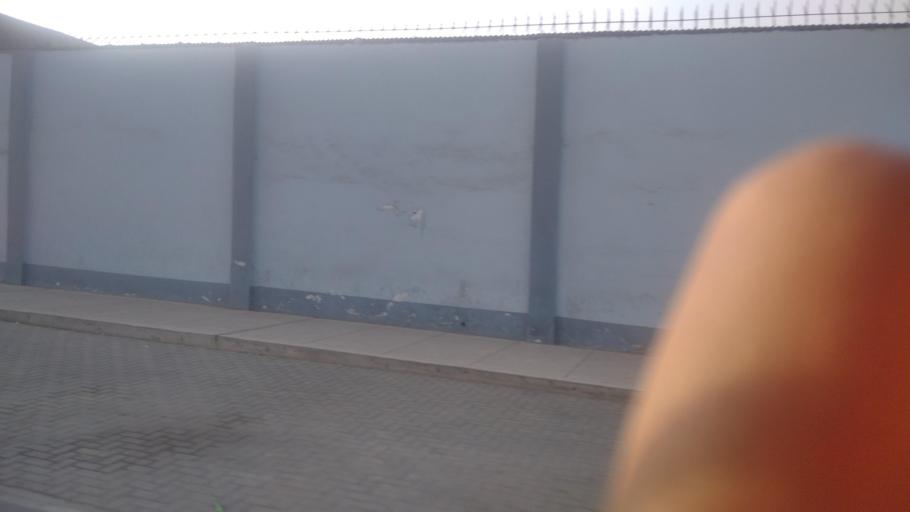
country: PE
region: Lima
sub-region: Lima
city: Vitarte
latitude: -12.0218
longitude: -76.9619
